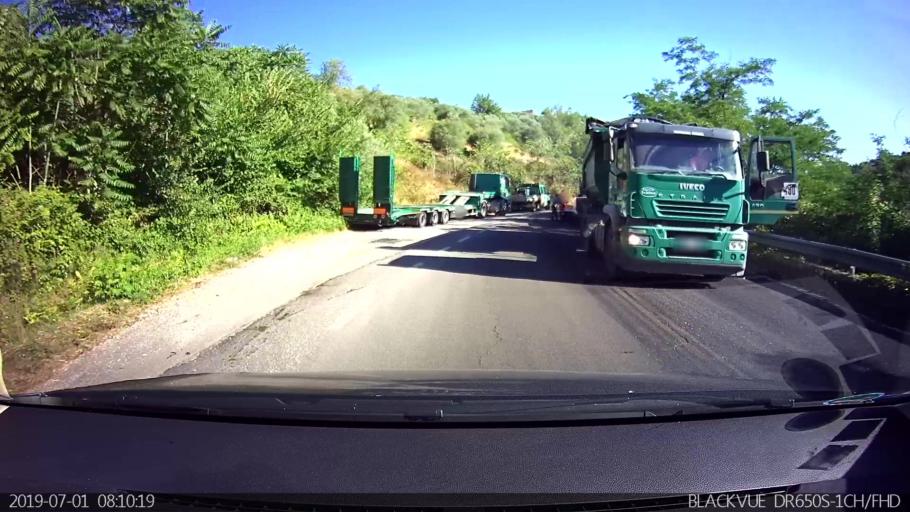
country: IT
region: Latium
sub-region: Provincia di Frosinone
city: Sant'Angelo in Villa-Giglio
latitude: 41.6696
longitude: 13.4217
